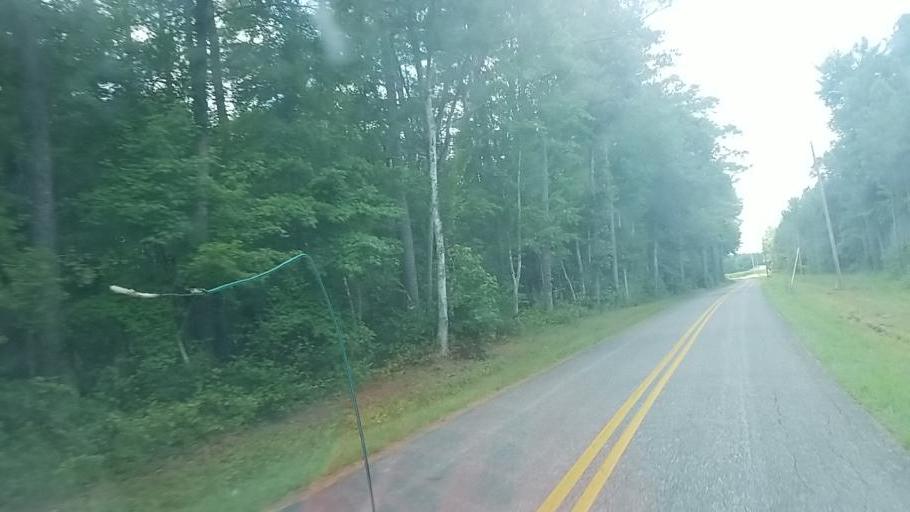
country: US
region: Maryland
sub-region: Worcester County
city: Snow Hill
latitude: 38.2584
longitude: -75.4475
